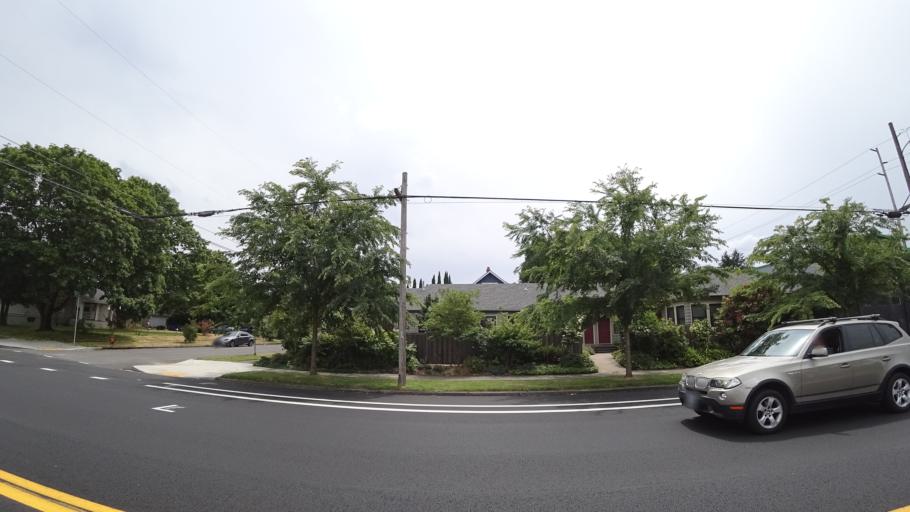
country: US
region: Oregon
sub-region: Multnomah County
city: Portland
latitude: 45.5700
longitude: -122.6948
